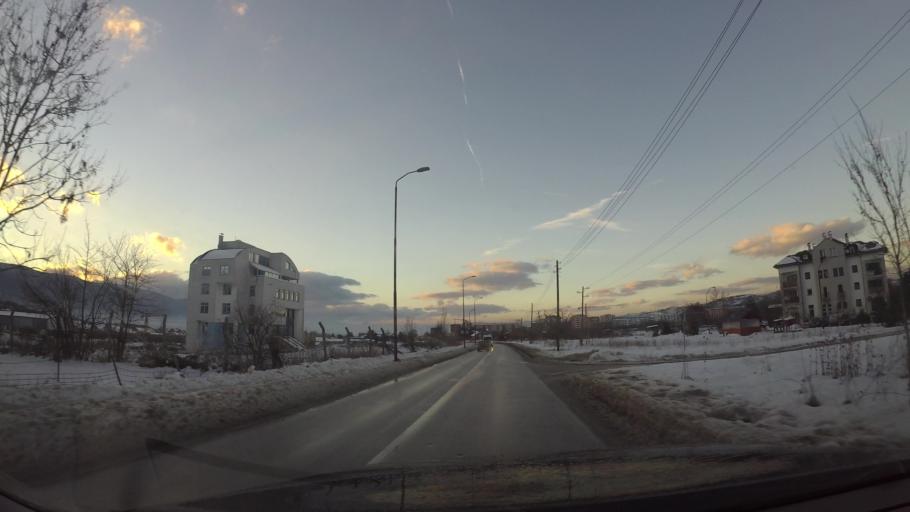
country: BA
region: Federation of Bosnia and Herzegovina
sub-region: Kanton Sarajevo
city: Sarajevo
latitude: 43.8131
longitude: 18.3685
